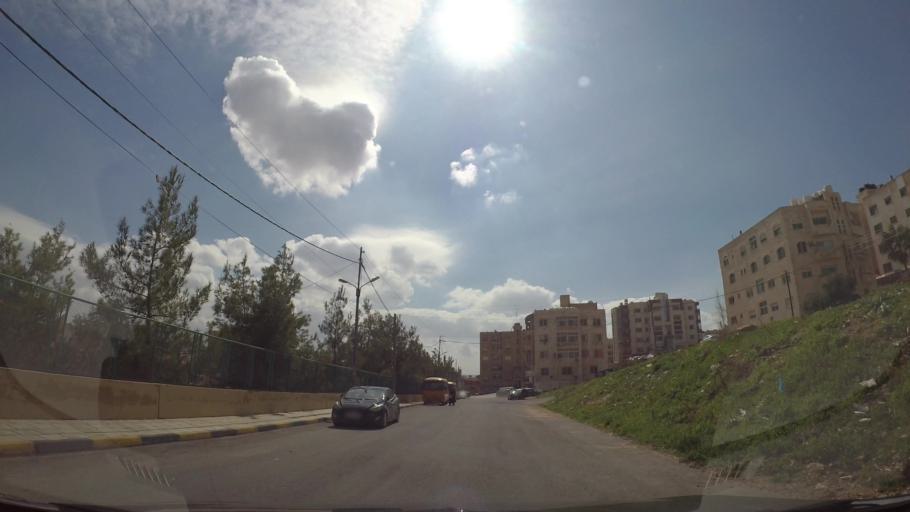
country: JO
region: Amman
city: Amman
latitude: 31.9911
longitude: 35.9076
